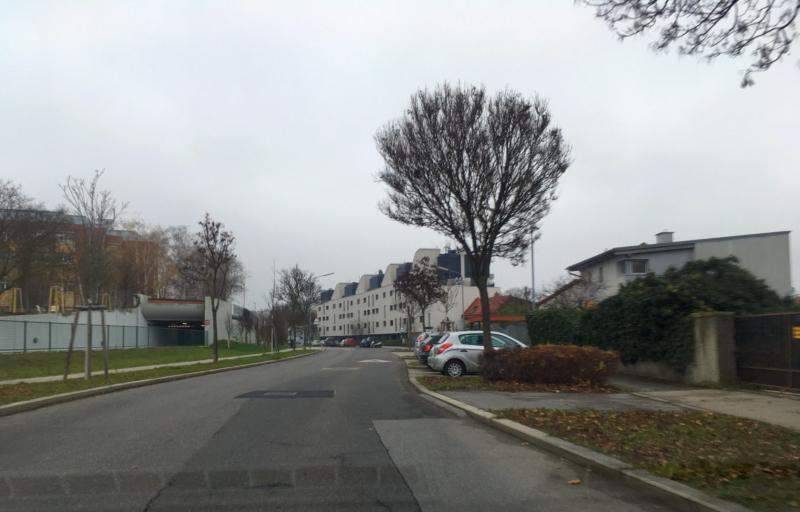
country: AT
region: Lower Austria
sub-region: Politischer Bezirk Wien-Umgebung
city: Gerasdorf bei Wien
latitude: 48.2187
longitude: 16.4604
